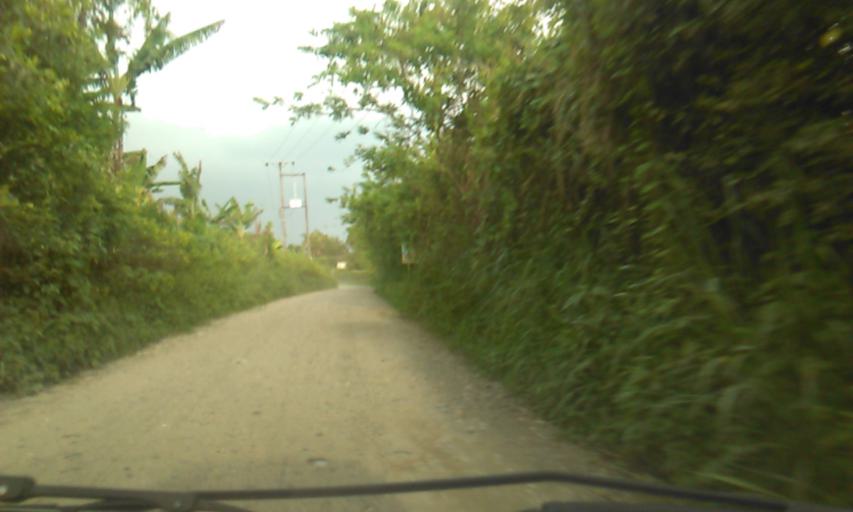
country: CO
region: Quindio
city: Montenegro
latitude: 4.5440
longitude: -75.7373
